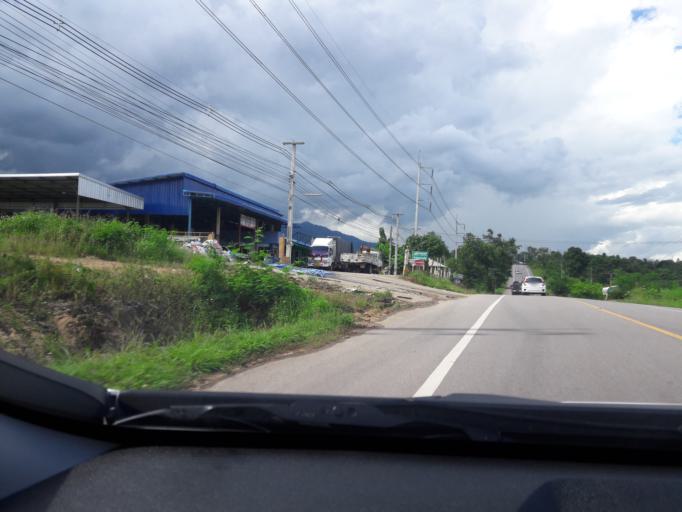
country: TH
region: Mae Hong Son
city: Mae Hi
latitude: 19.3305
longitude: 98.4343
